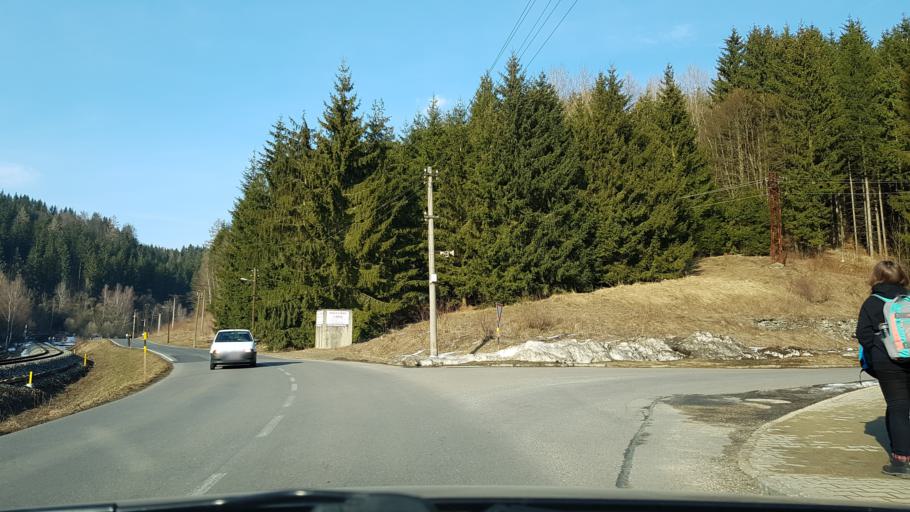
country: CZ
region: Olomoucky
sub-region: Okres Sumperk
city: Hanusovice
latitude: 50.1033
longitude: 16.9954
